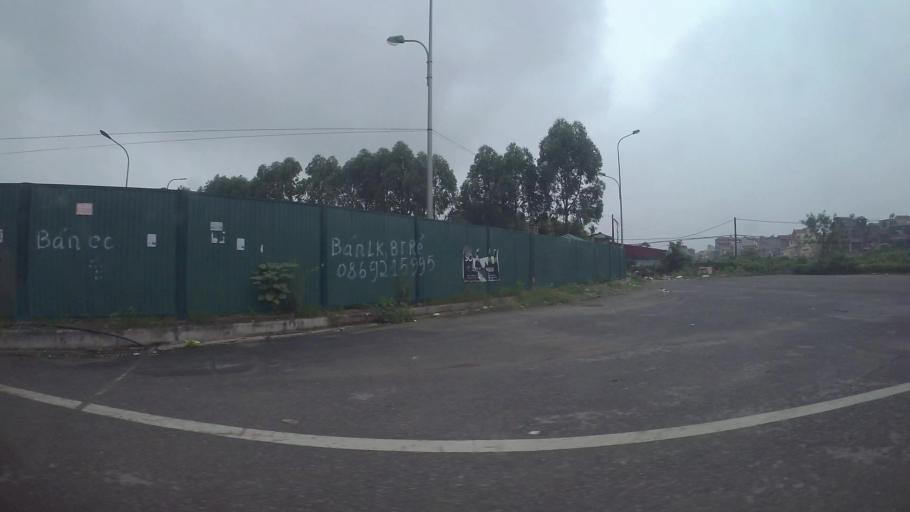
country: VN
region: Ha Noi
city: Van Dien
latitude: 20.9686
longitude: 105.8753
